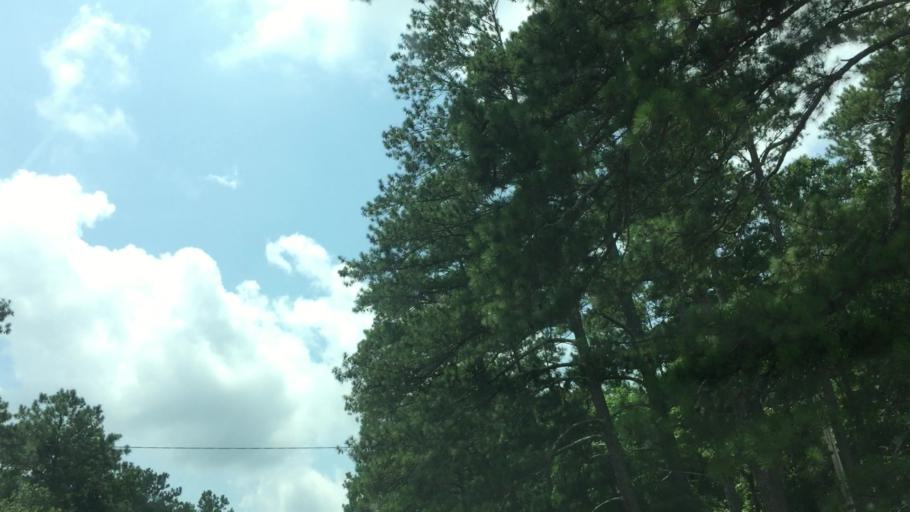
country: US
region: Georgia
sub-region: Carroll County
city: Carrollton
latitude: 33.6113
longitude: -84.9645
